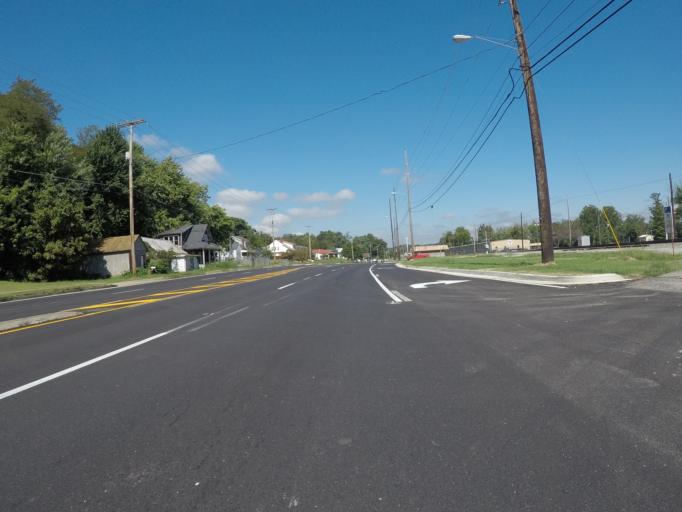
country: US
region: Ohio
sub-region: Lawrence County
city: South Point
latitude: 38.4332
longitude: -82.6054
